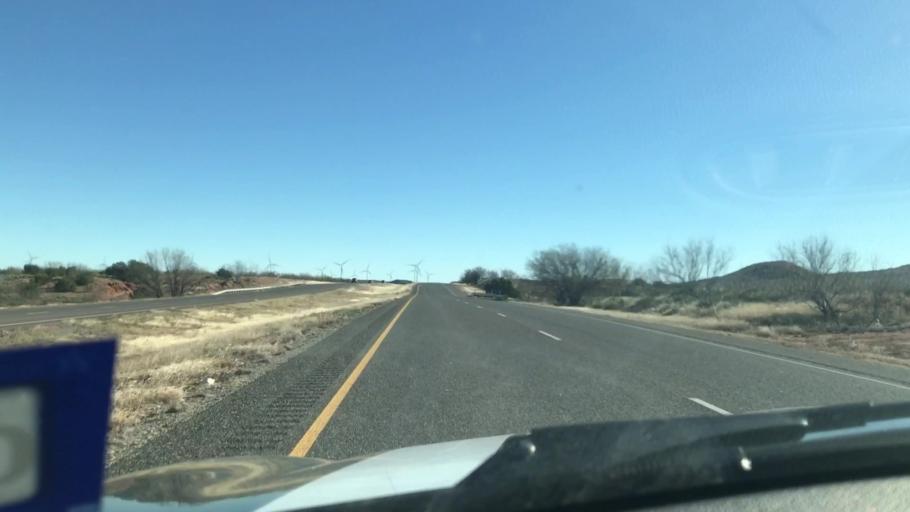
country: US
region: Texas
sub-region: Scurry County
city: Snyder
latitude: 32.9372
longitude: -101.0741
